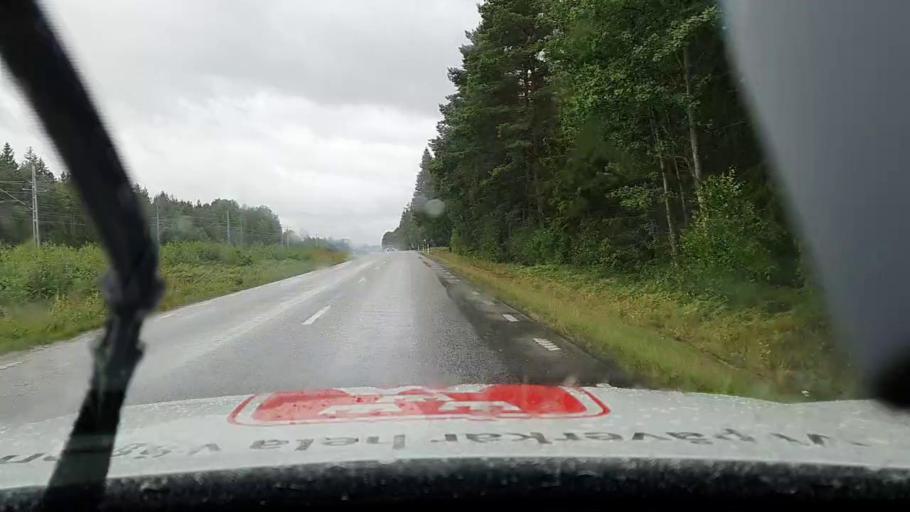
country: SE
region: Vaestra Goetaland
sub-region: Toreboda Kommun
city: Toereboda
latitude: 58.6669
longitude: 14.0926
